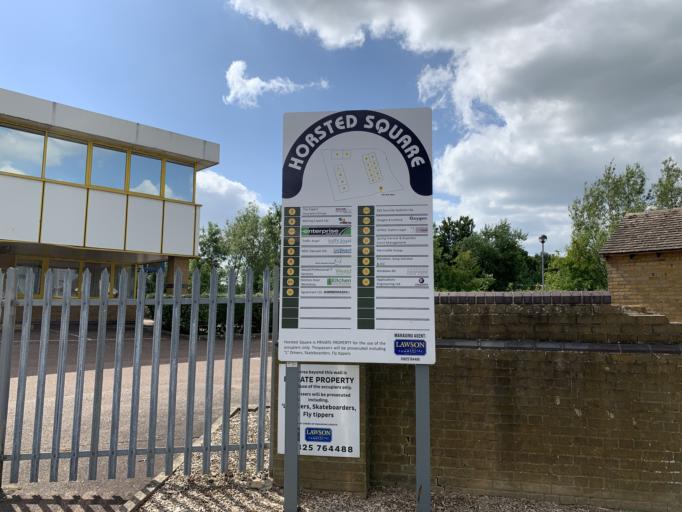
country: GB
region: England
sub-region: East Sussex
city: Uckfield
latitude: 50.9664
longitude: 0.0829
